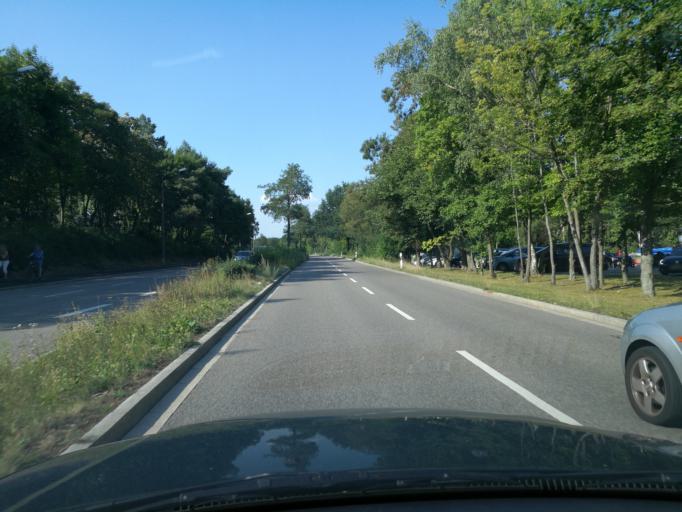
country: DE
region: Bavaria
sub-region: Regierungsbezirk Mittelfranken
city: Erlangen
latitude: 49.5962
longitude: 10.9703
